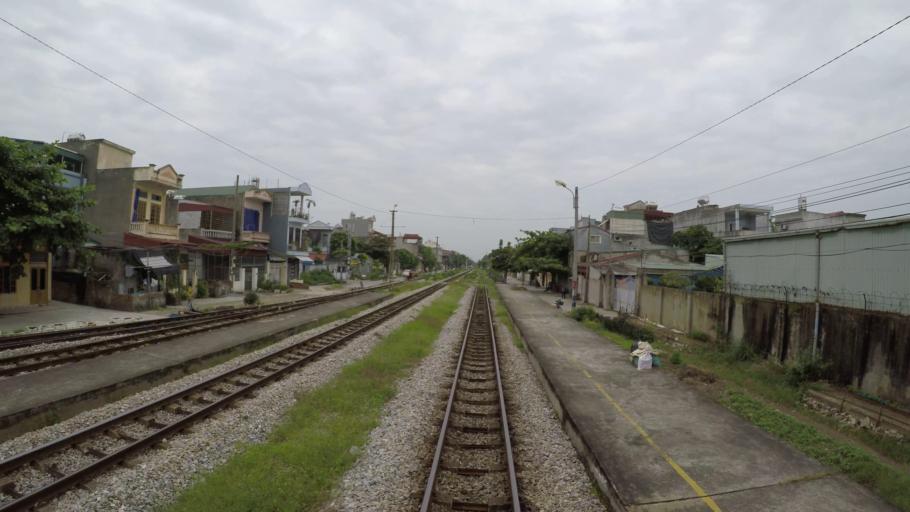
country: VN
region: Hai Duong
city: Thanh Pho Hai Duong
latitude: 20.9426
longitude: 106.3056
